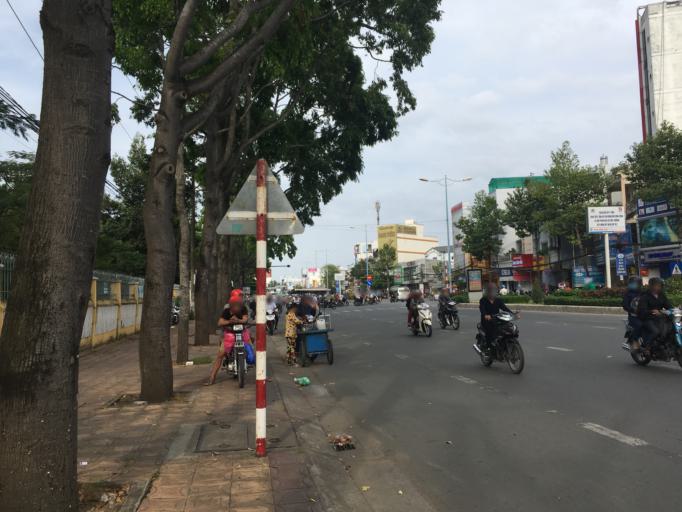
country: VN
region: Can Tho
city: Can Tho
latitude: 10.0297
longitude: 105.7718
